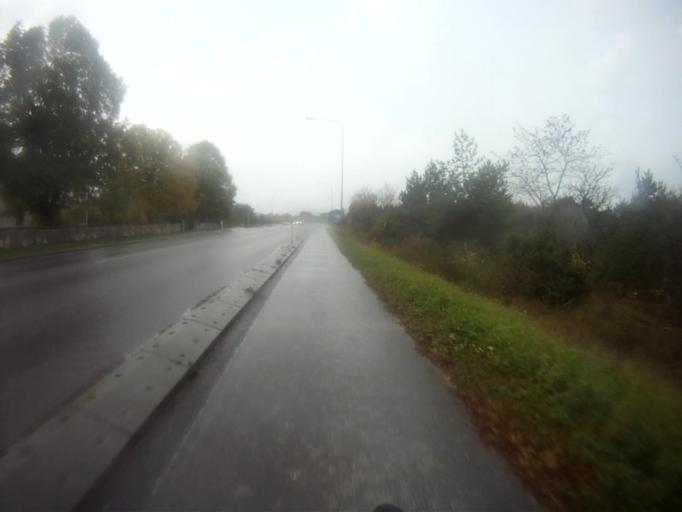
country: SE
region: Gotland
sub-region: Gotland
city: Visby
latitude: 57.6524
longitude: 18.3184
